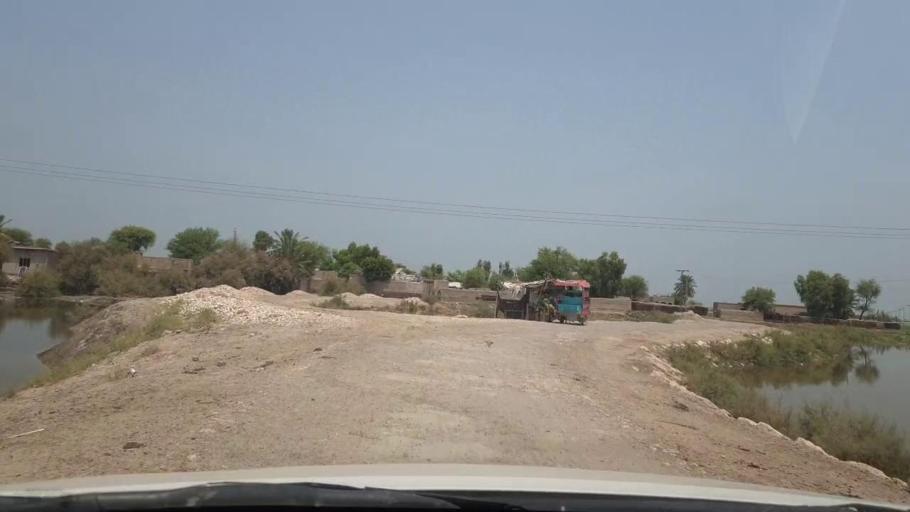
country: PK
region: Sindh
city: Rustam jo Goth
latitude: 28.0160
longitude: 68.7836
